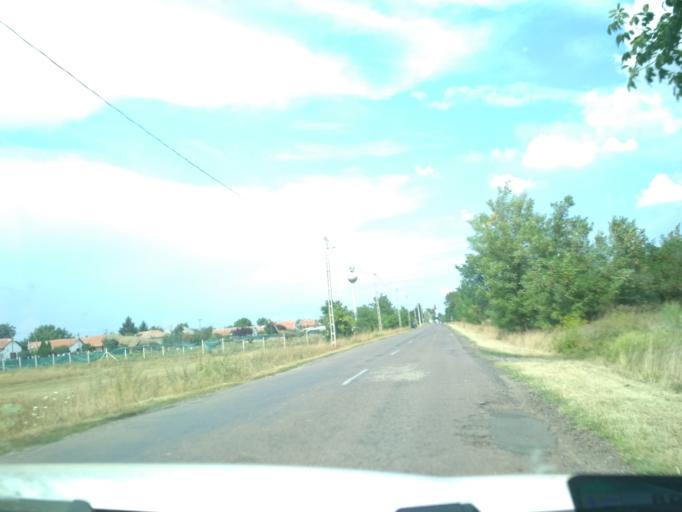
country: HU
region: Jasz-Nagykun-Szolnok
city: Abadszalok
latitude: 47.5070
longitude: 20.6342
